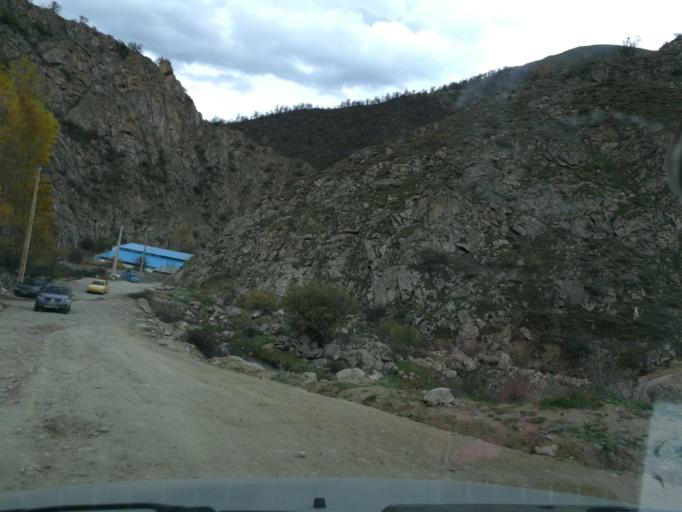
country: IR
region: Mazandaran
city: `Abbasabad
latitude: 36.4380
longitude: 51.0602
